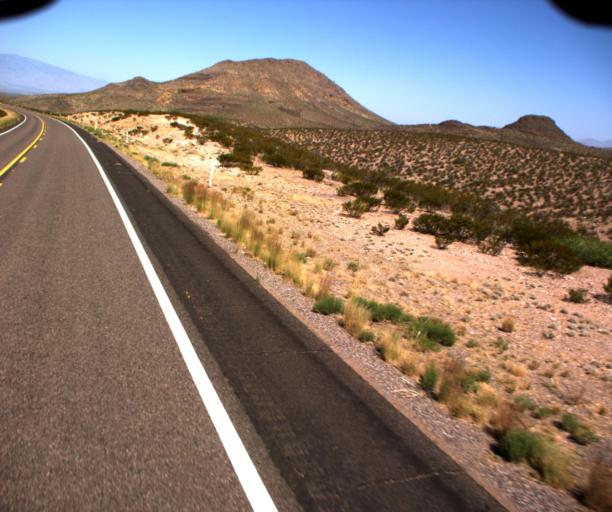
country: US
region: Arizona
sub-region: Greenlee County
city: Clifton
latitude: 32.7542
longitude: -109.3668
